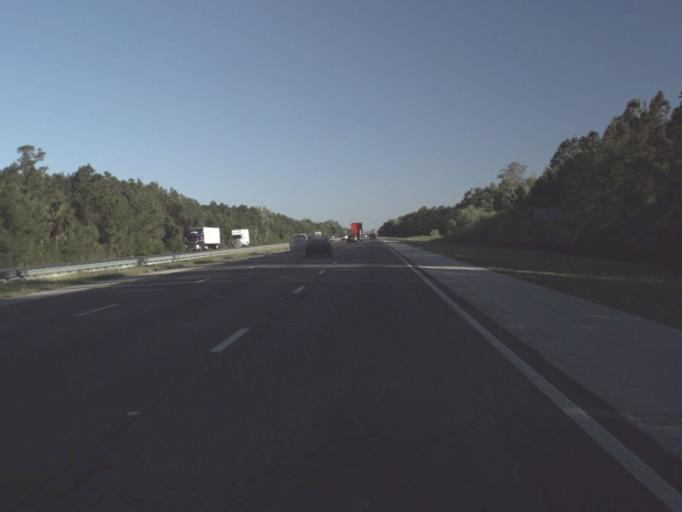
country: US
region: Florida
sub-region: Flagler County
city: Palm Coast
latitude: 29.6253
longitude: -81.2622
